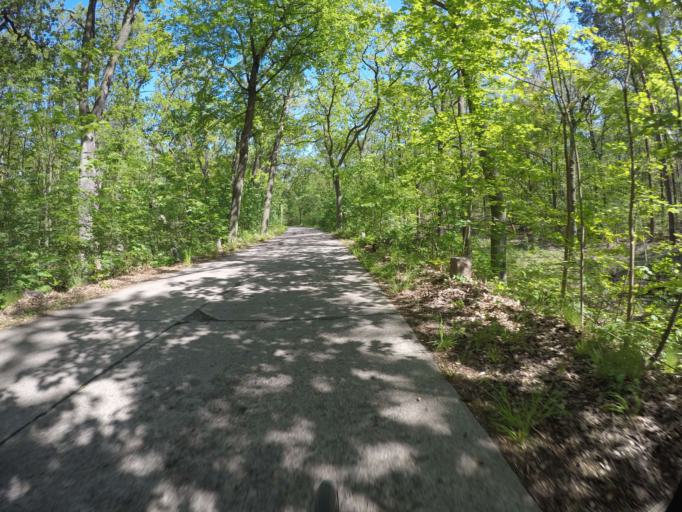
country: DE
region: Berlin
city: Wannsee
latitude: 52.4255
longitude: 13.1336
